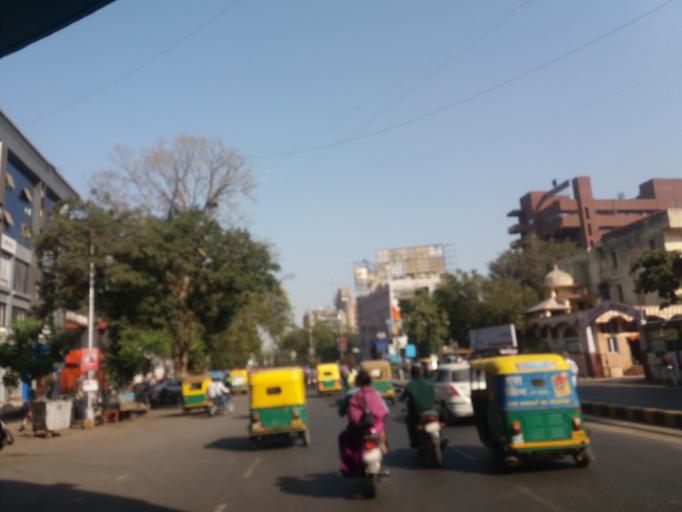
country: IN
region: Gujarat
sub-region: Ahmadabad
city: Ahmedabad
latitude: 23.0236
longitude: 72.5712
